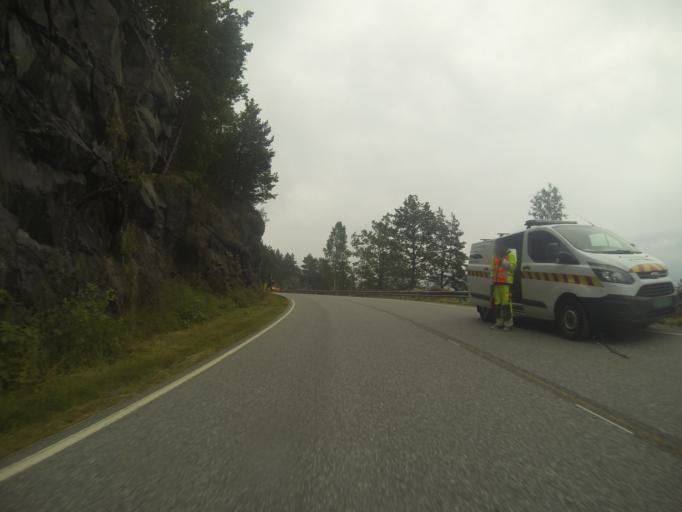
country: NO
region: Rogaland
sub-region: Suldal
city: Sand
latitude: 59.5333
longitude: 6.2547
